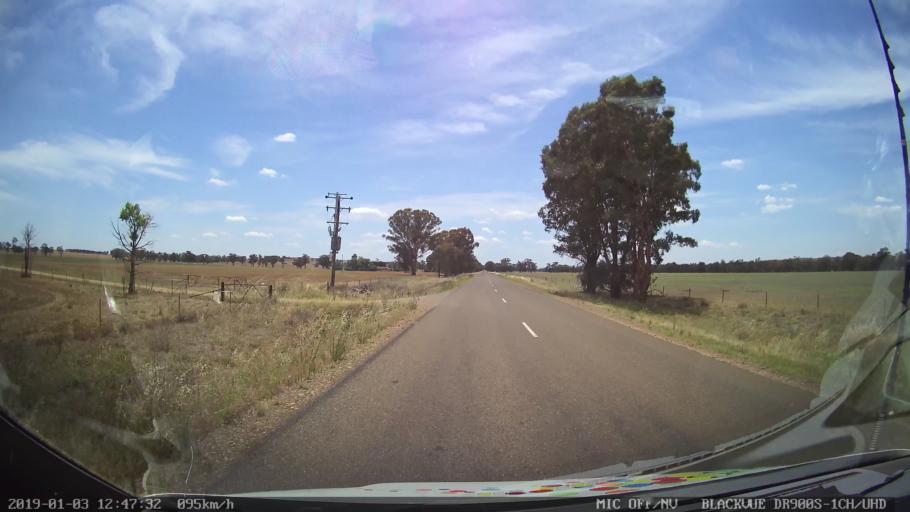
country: AU
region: New South Wales
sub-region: Weddin
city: Grenfell
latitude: -33.7257
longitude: 148.2427
